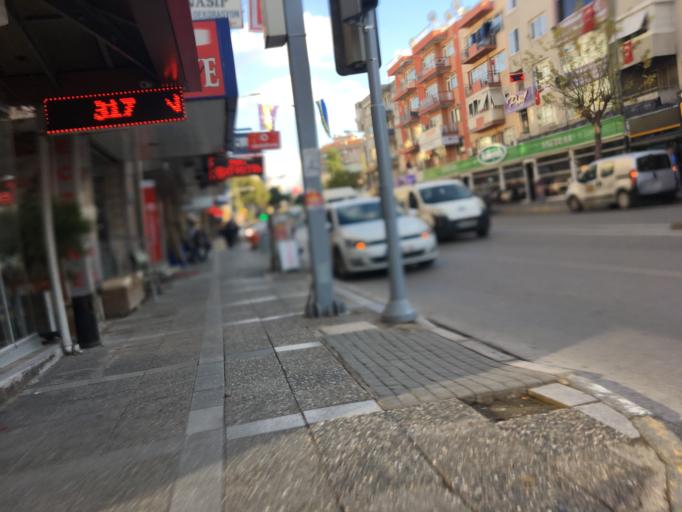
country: TR
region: Izmir
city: Buca
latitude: 38.3901
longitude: 27.1656
